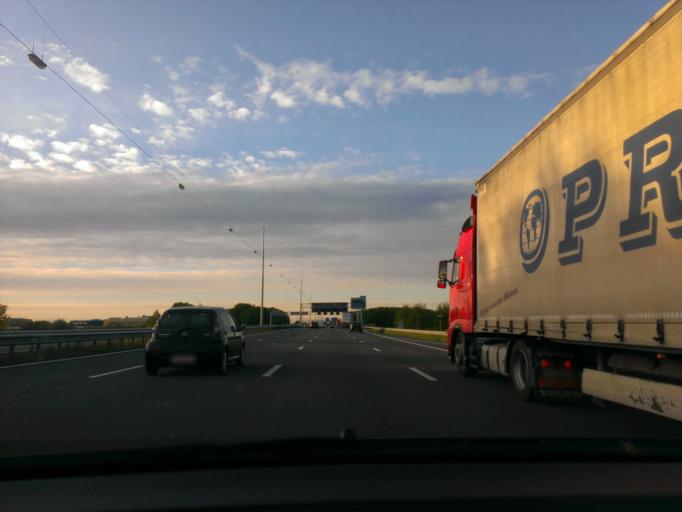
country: NL
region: South Holland
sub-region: Gemeente Barendrecht
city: Barendrecht
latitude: 51.8429
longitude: 4.5155
